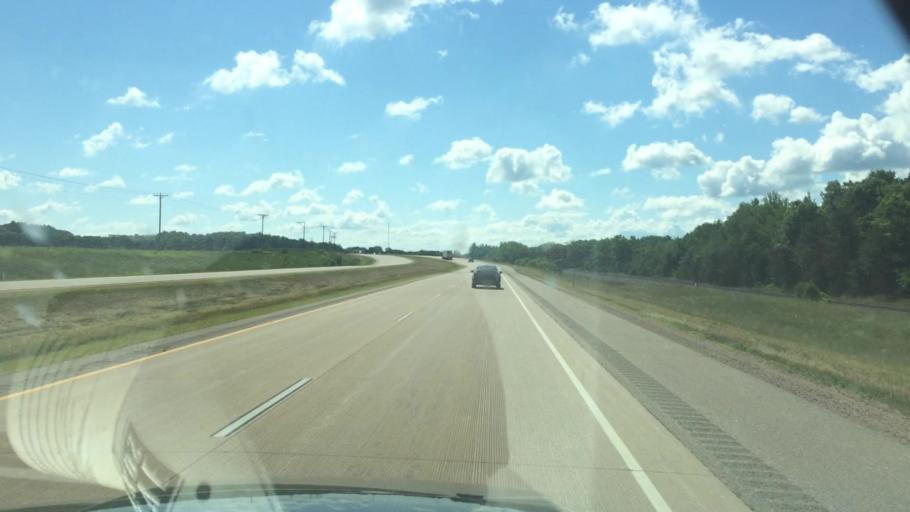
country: US
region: Wisconsin
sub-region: Portage County
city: Amherst
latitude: 44.4780
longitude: -89.3346
